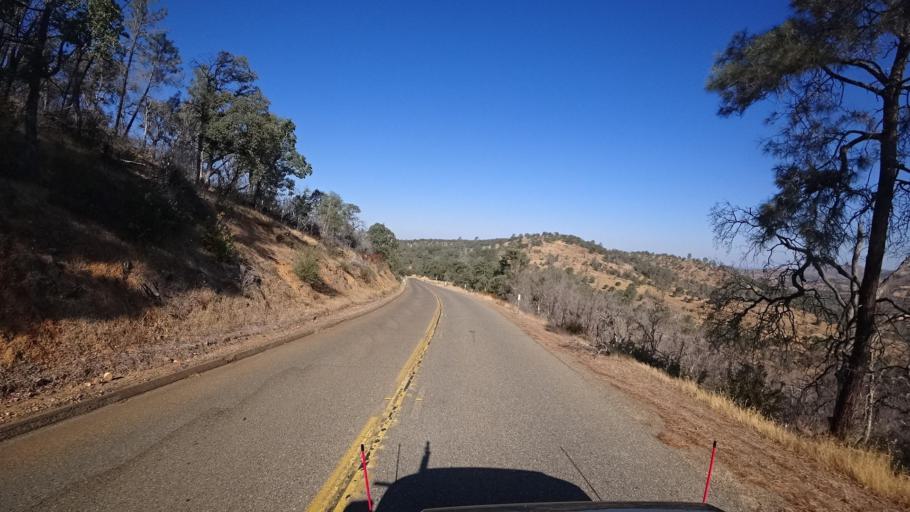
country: US
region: California
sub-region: Mariposa County
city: Mariposa
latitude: 37.5650
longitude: -120.1659
